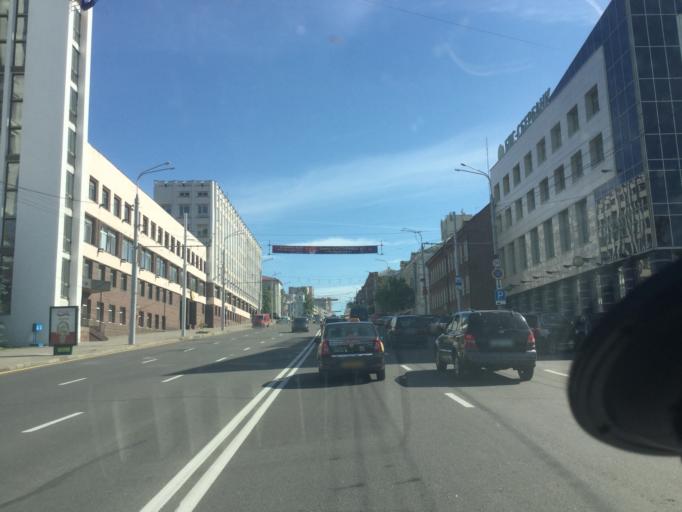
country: BY
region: Vitebsk
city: Vitebsk
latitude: 55.1910
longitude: 30.2060
